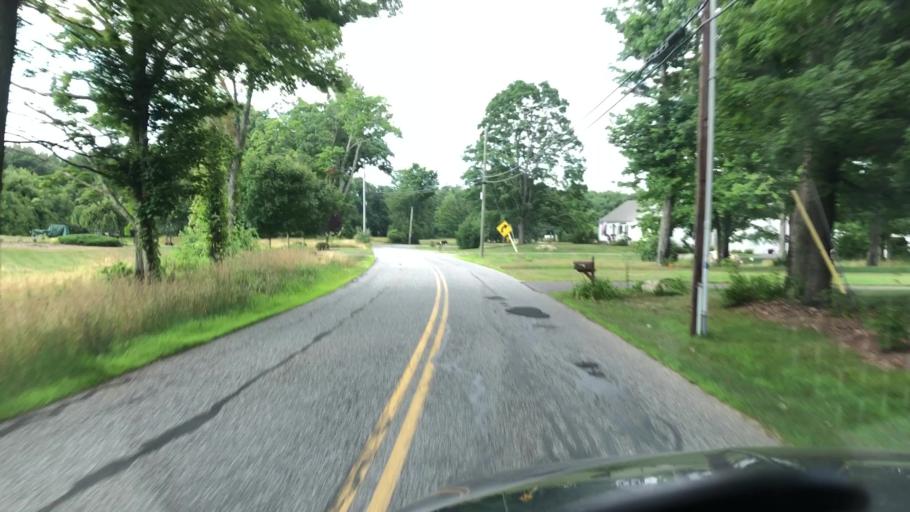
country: US
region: Massachusetts
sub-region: Hampshire County
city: Southampton
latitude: 42.2360
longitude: -72.6940
